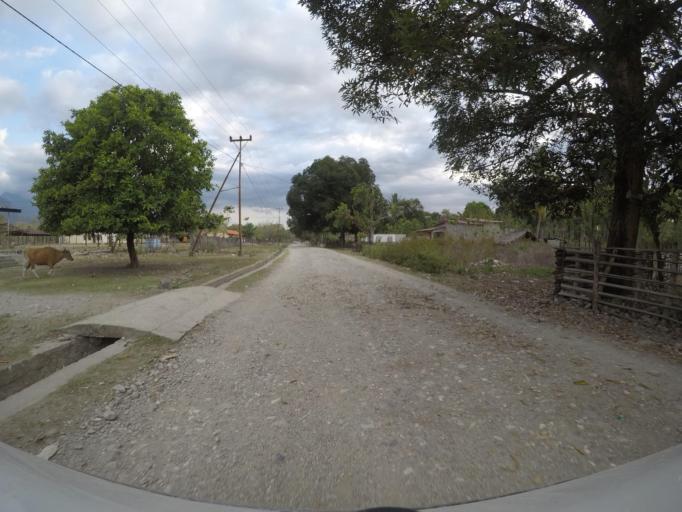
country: TL
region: Bobonaro
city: Maliana
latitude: -8.8696
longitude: 125.2131
